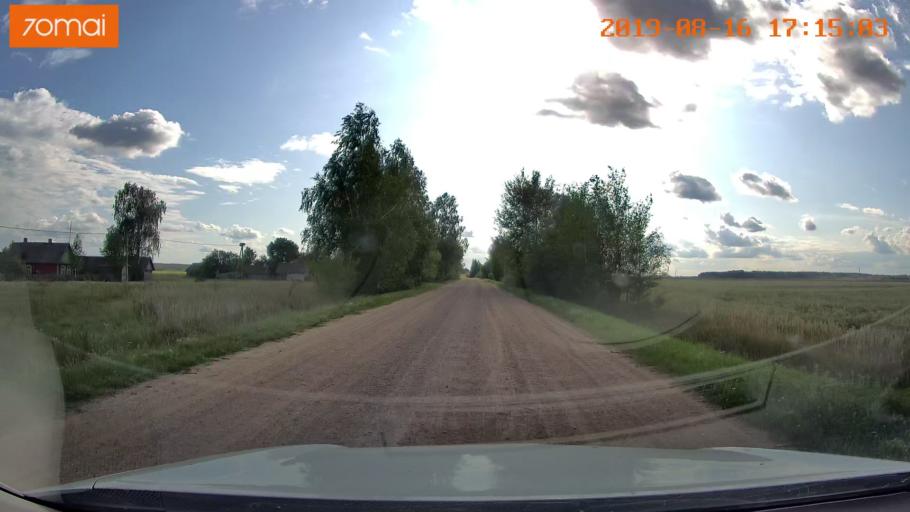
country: BY
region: Mogilev
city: Hlusha
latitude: 53.1810
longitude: 28.8488
